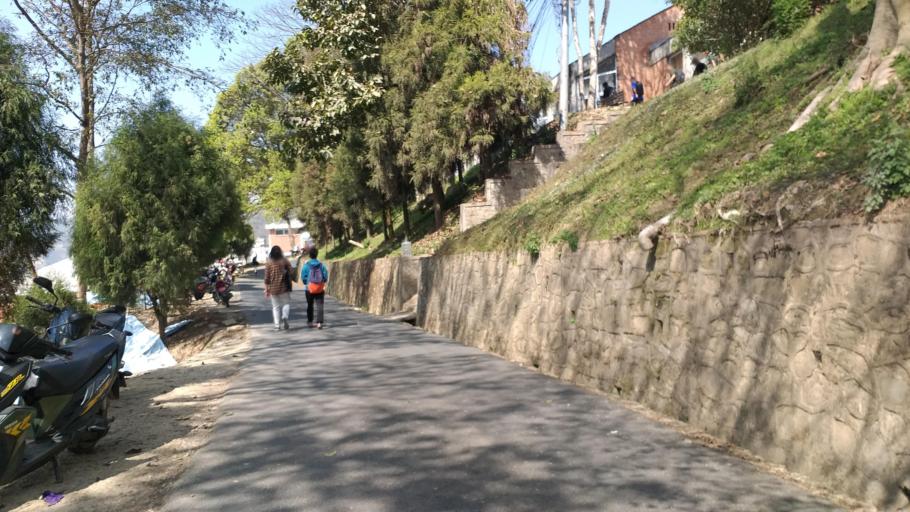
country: NP
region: Central Region
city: Banepa
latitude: 27.6190
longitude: 85.5378
